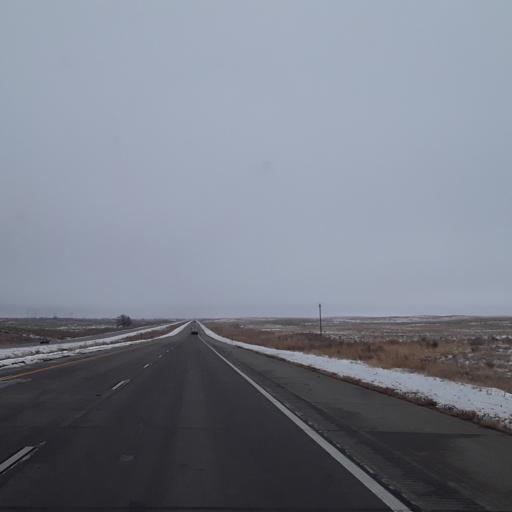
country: US
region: Colorado
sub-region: Logan County
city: Sterling
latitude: 40.5628
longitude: -103.2094
